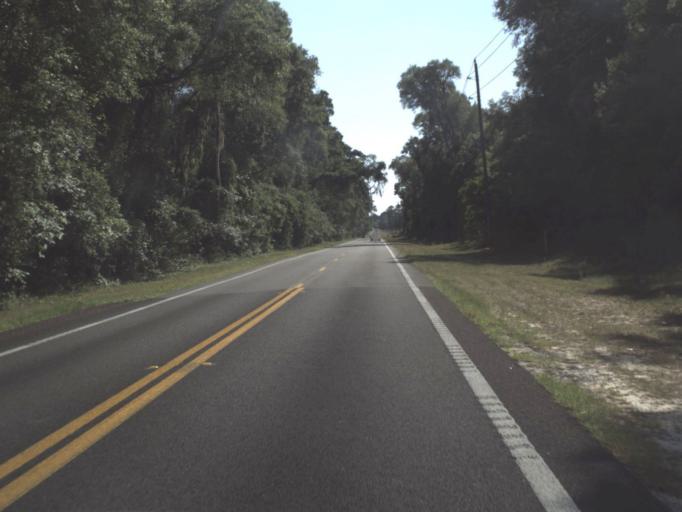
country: US
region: Florida
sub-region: Marion County
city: Ocala
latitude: 29.1800
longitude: -82.3189
